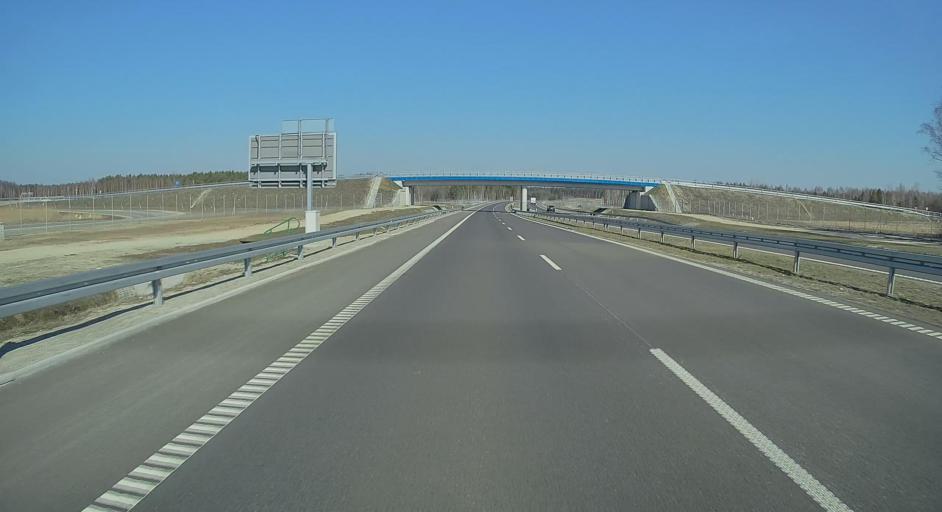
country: PL
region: Subcarpathian Voivodeship
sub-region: Powiat nizanski
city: Jarocin
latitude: 50.5825
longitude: 22.2524
